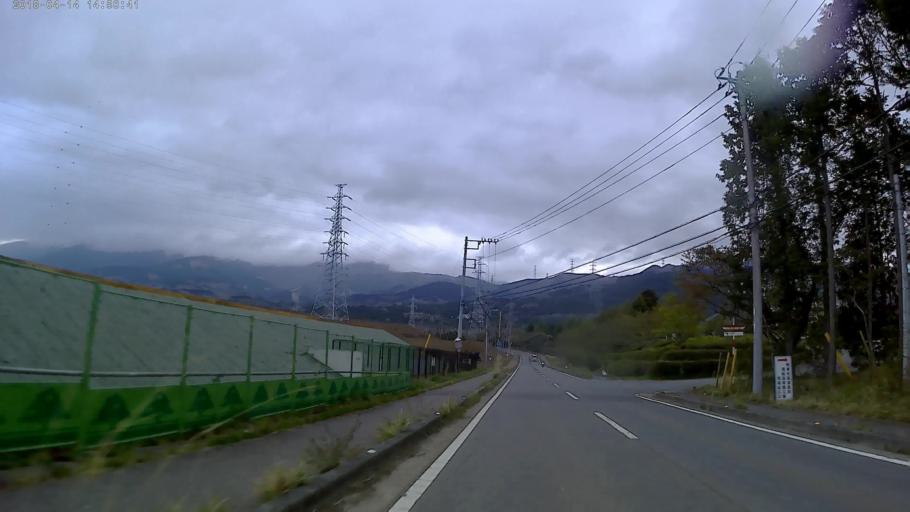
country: JP
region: Shizuoka
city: Gotemba
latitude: 35.3680
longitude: 138.9649
